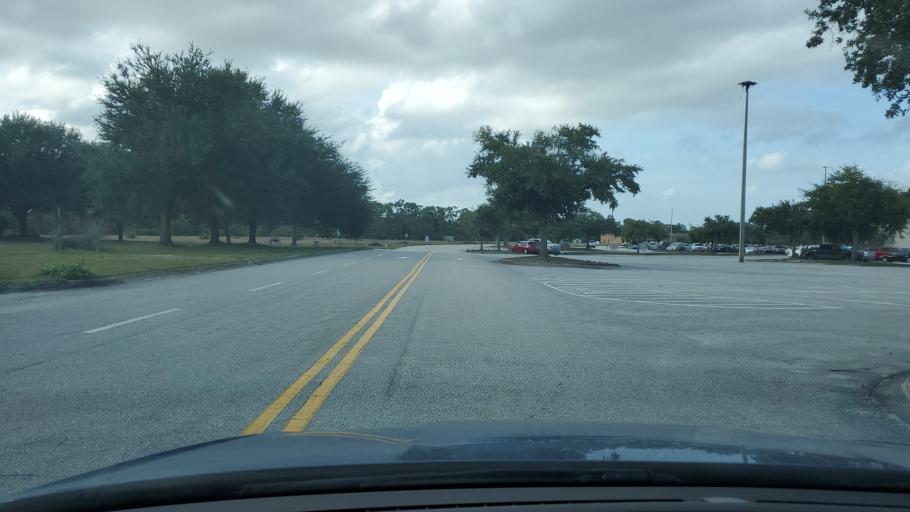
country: US
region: Florida
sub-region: Highlands County
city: Sebring
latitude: 27.4880
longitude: -81.4877
